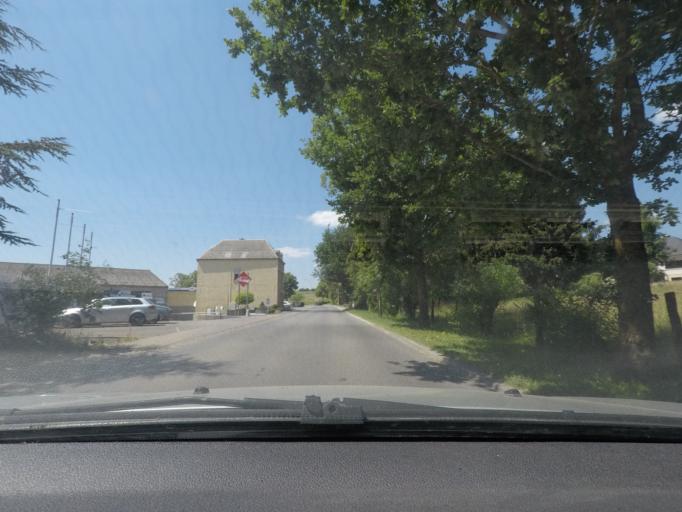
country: LU
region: Diekirch
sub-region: Canton de Redange
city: Redange-sur-Attert
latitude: 49.7665
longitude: 5.8773
